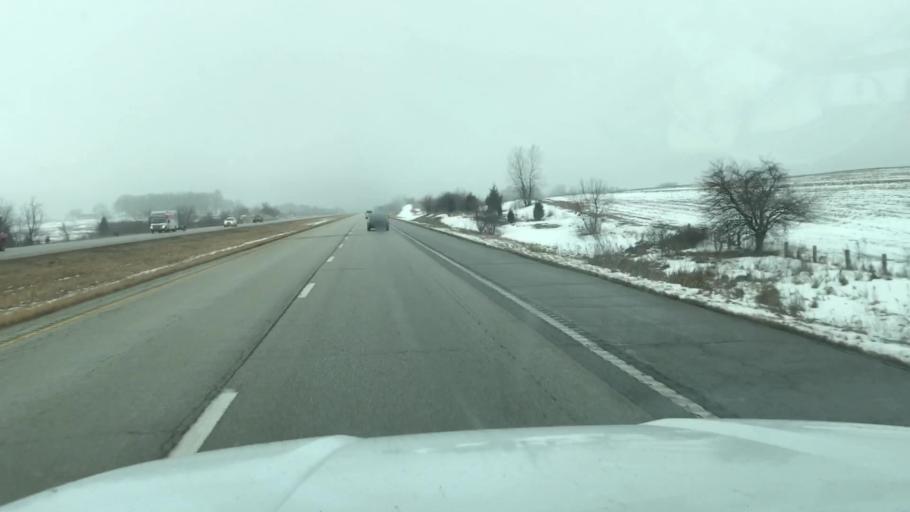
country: US
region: Missouri
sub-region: Andrew County
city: Country Club Village
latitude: 39.7478
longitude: -94.6878
